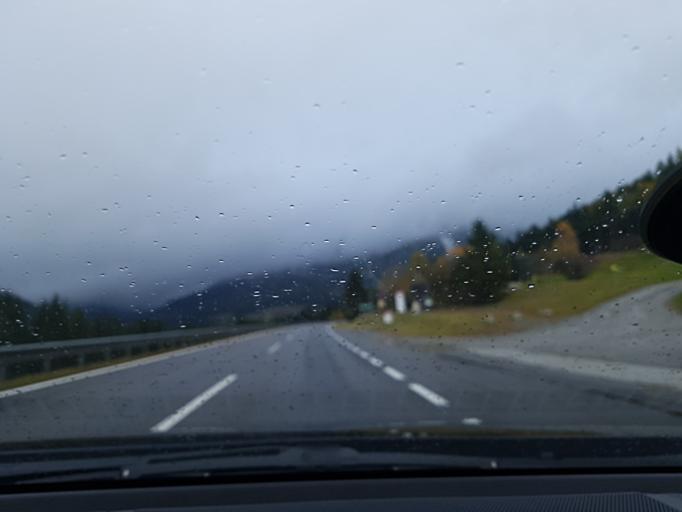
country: AT
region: Styria
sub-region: Politischer Bezirk Murtal
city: Hohentauern
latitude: 47.4261
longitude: 14.4634
